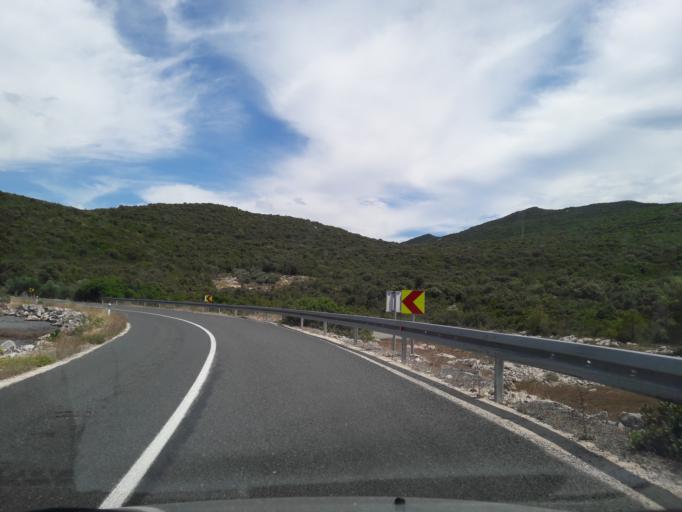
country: HR
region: Dubrovacko-Neretvanska
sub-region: Grad Dubrovnik
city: Opuzen
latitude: 42.9147
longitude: 17.4683
